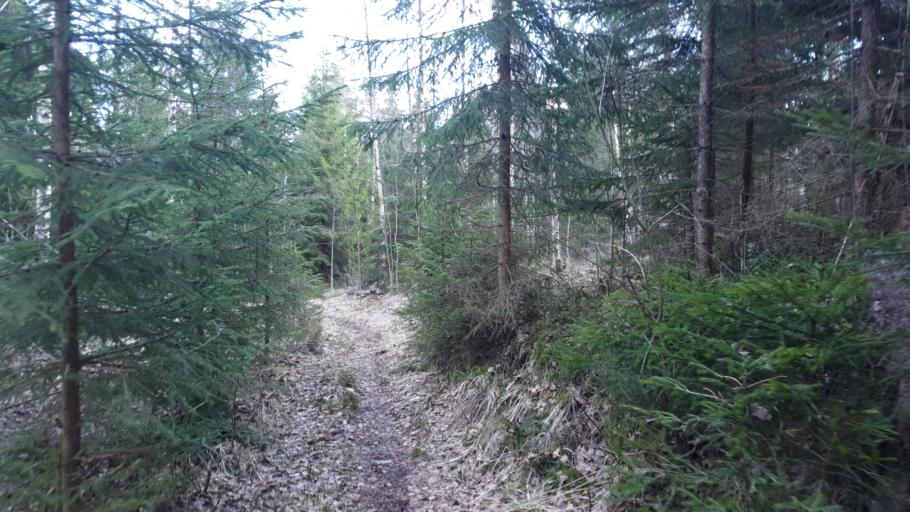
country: SE
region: OErebro
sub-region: Orebro Kommun
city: Garphyttan
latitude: 59.3690
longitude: 14.9739
